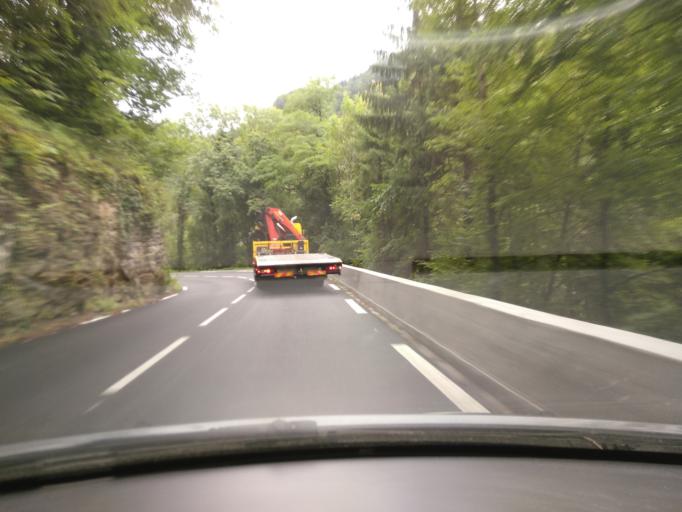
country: FR
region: Rhone-Alpes
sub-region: Departement de la Haute-Savoie
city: Bonneville
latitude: 46.0428
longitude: 6.3795
